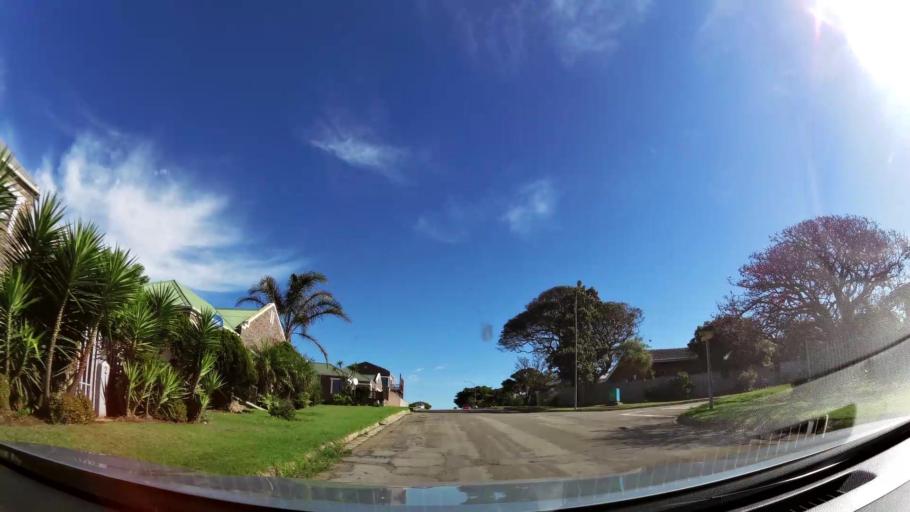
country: ZA
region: Eastern Cape
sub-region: Cacadu District Municipality
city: Jeffrey's Bay
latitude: -34.0517
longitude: 24.9171
